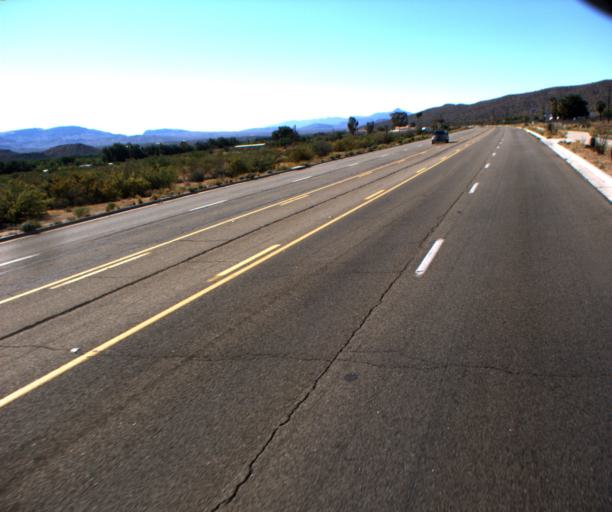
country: US
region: Arizona
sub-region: Yavapai County
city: Bagdad
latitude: 34.7084
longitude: -113.6130
